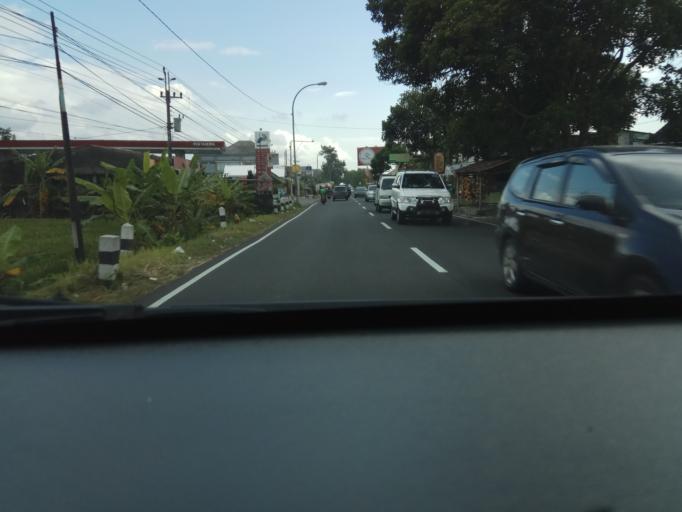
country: ID
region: Daerah Istimewa Yogyakarta
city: Melati
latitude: -7.7102
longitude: 110.4093
